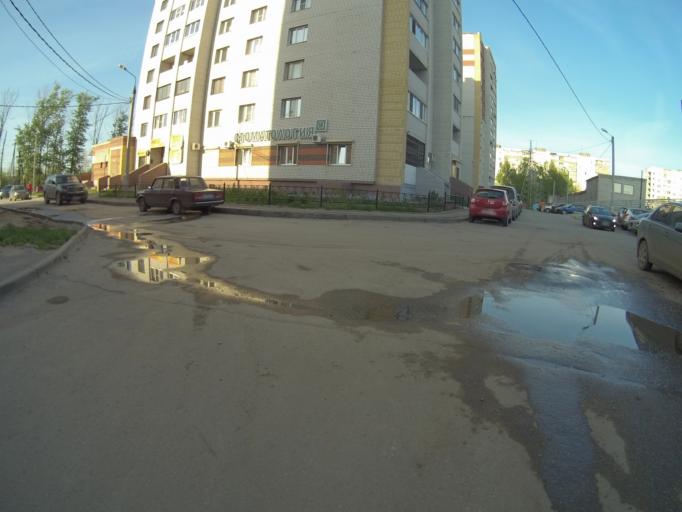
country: RU
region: Vladimir
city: Kommunar
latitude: 56.1724
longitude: 40.4506
